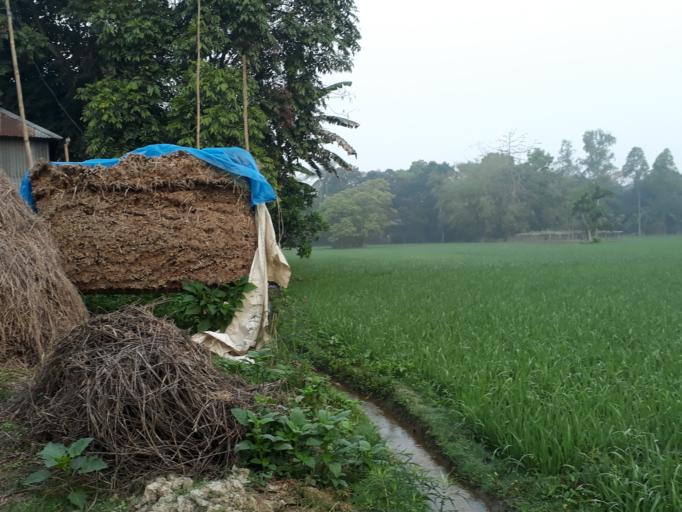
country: BD
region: Rajshahi
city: Sirajganj
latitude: 24.3233
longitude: 89.6733
